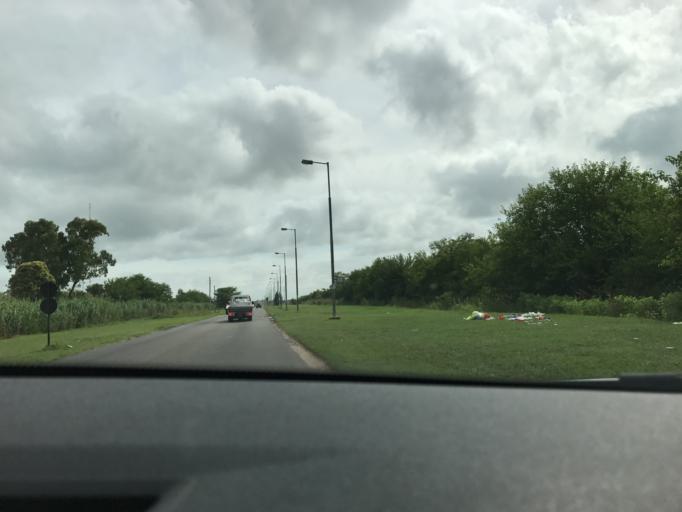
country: AR
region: Buenos Aires
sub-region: Partido de La Plata
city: La Plata
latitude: -34.8460
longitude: -58.0767
